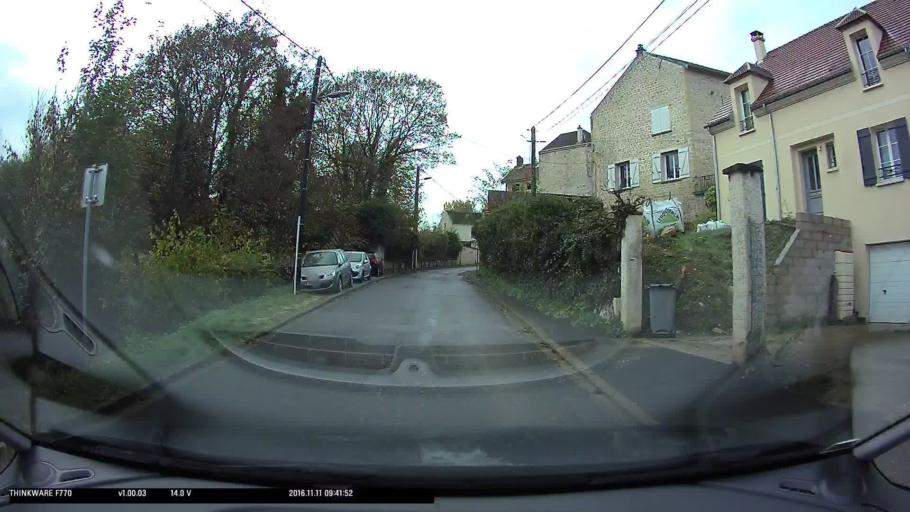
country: FR
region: Ile-de-France
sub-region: Departement du Val-d'Oise
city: Osny
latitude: 49.0684
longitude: 2.0570
